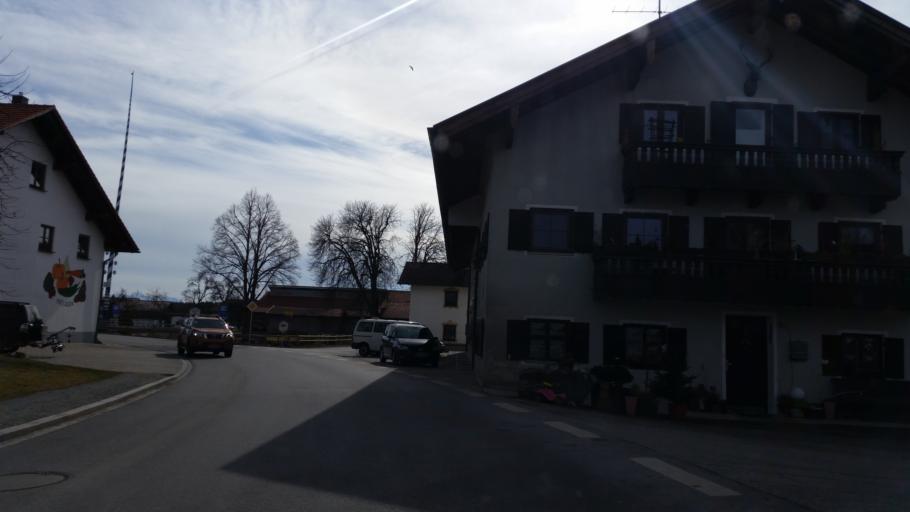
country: DE
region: Bavaria
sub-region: Upper Bavaria
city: Glonn
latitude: 48.0055
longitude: 11.8440
